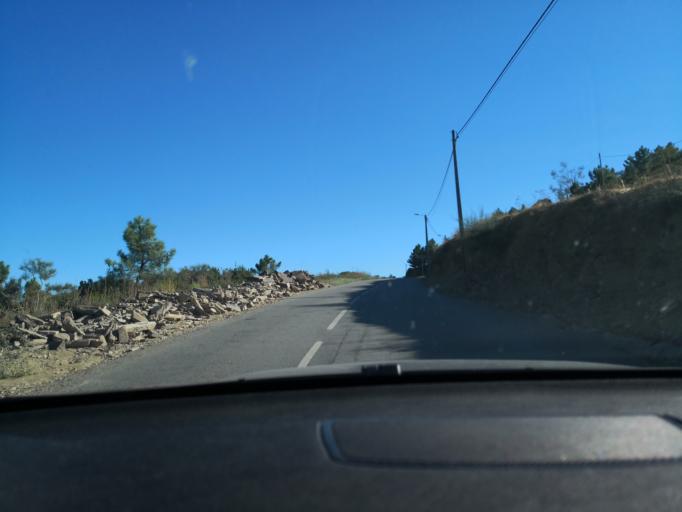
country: PT
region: Vila Real
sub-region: Sabrosa
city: Vilela
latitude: 41.2252
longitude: -7.5631
